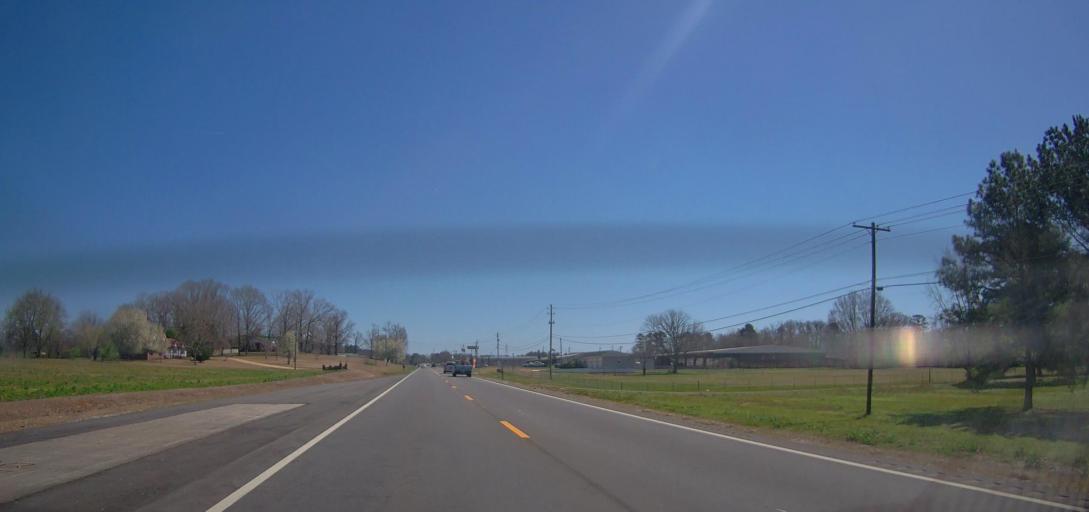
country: US
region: Alabama
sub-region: Calhoun County
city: Alexandria
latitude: 33.7824
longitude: -85.9034
